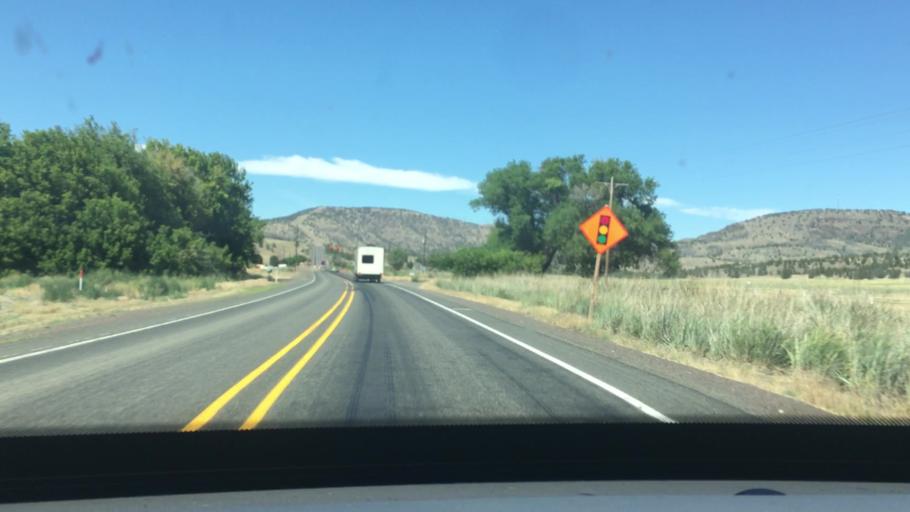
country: US
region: Oregon
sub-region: Jefferson County
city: Madras
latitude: 44.8077
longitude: -120.9343
